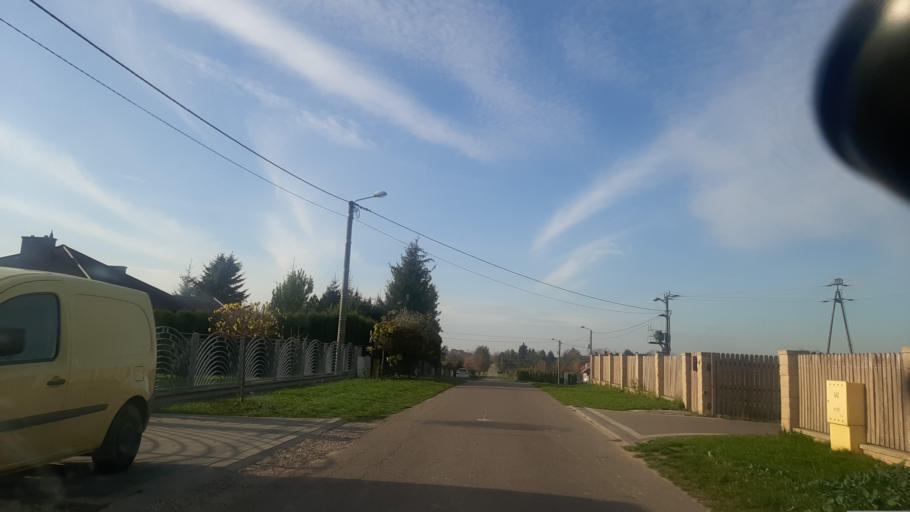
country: PL
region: Lublin Voivodeship
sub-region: Powiat pulawski
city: Markuszow
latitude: 51.3633
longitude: 22.2903
